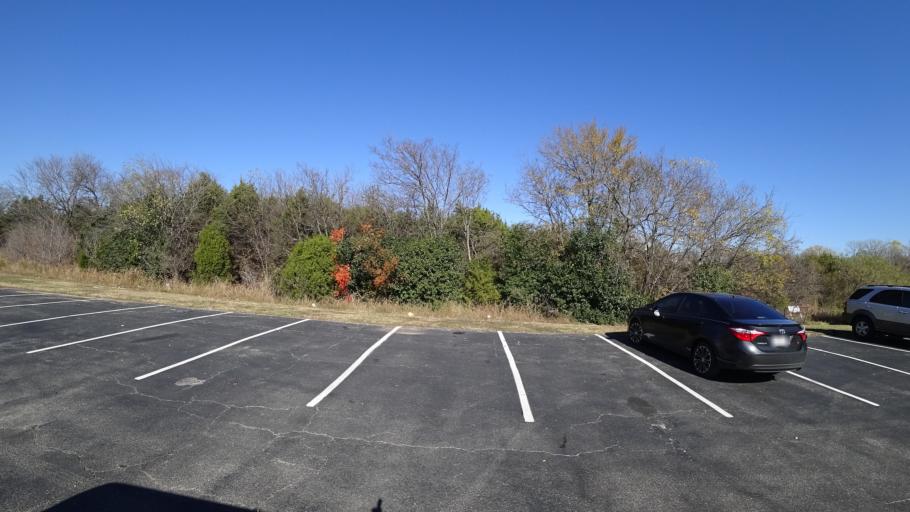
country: US
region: Texas
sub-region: Travis County
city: Wells Branch
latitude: 30.4237
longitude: -97.7003
